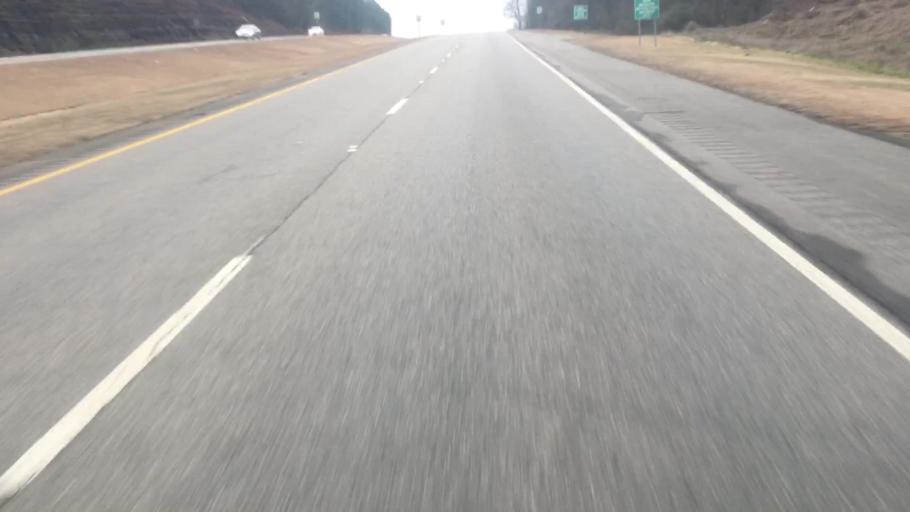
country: US
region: Alabama
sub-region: Walker County
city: Sumiton
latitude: 33.7672
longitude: -87.0707
